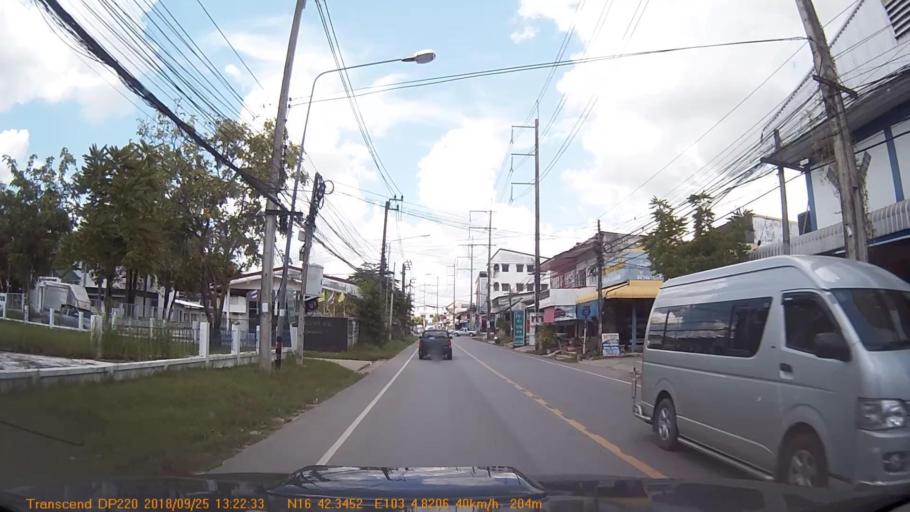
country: TH
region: Khon Kaen
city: Kranuan
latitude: 16.7060
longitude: 103.0805
